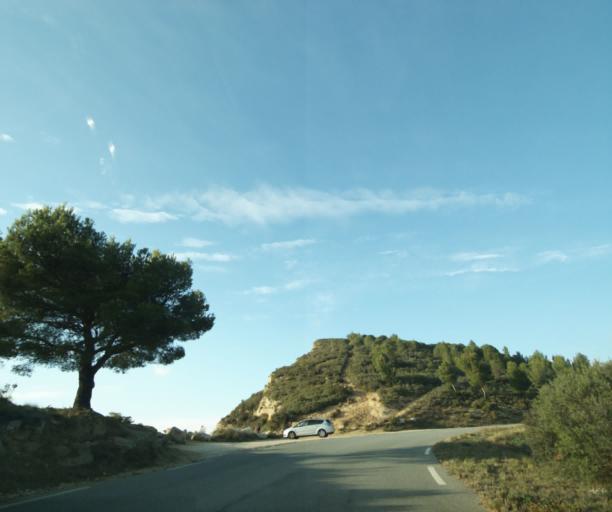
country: FR
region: Provence-Alpes-Cote d'Azur
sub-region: Departement des Bouches-du-Rhone
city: Cassis
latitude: 43.1909
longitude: 5.5556
